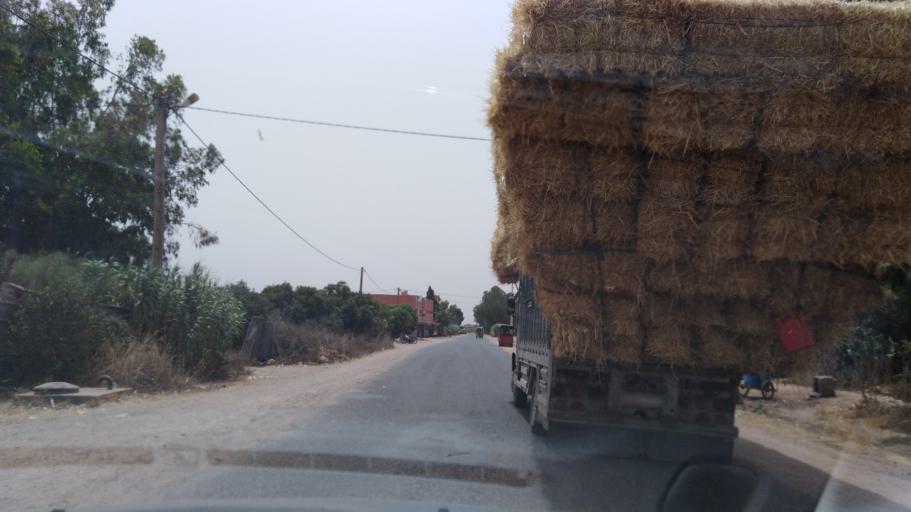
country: MA
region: Grand Casablanca
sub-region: Mediouna
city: Mediouna
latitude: 33.4010
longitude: -7.5122
